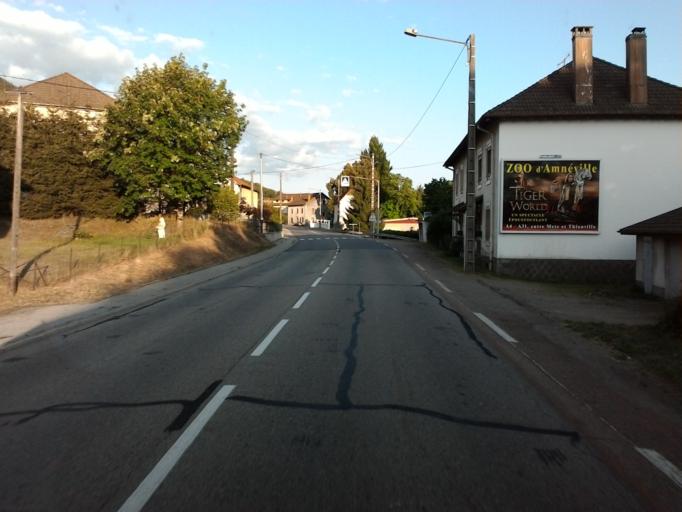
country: FR
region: Lorraine
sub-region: Departement des Vosges
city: Ramonchamp
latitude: 47.9075
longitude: 6.7077
